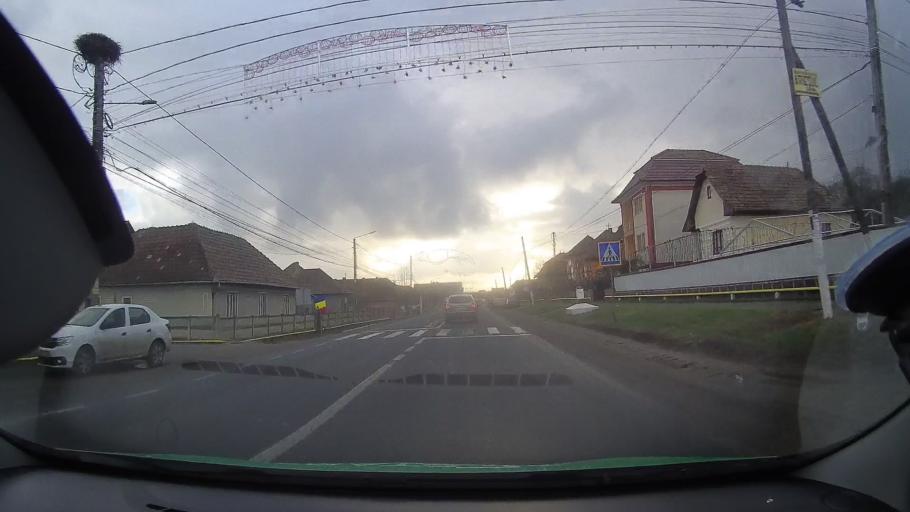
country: RO
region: Cluj
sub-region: Comuna Luna
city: Luncani
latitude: 46.5040
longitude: 23.9197
